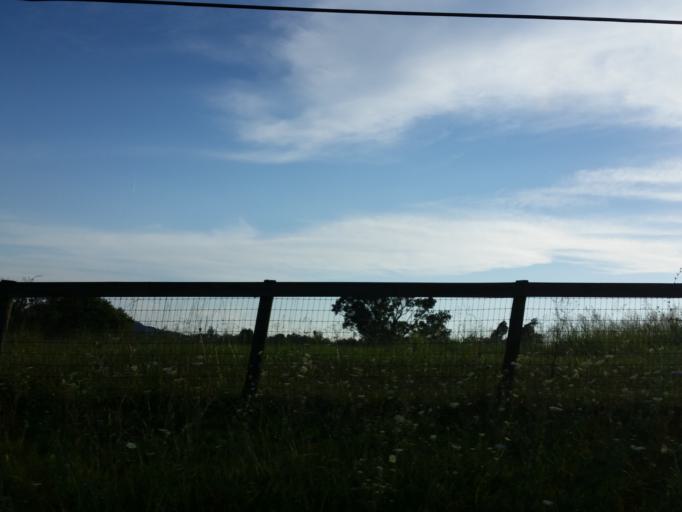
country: US
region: Tennessee
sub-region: Blount County
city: Eagleton Village
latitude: 35.8749
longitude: -83.9268
